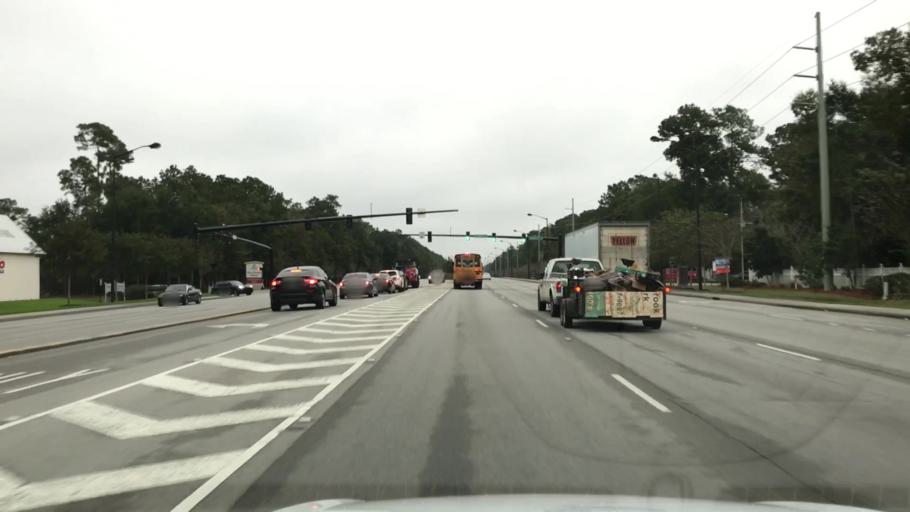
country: US
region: South Carolina
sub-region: Charleston County
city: Isle of Palms
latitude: 32.8749
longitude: -79.7716
